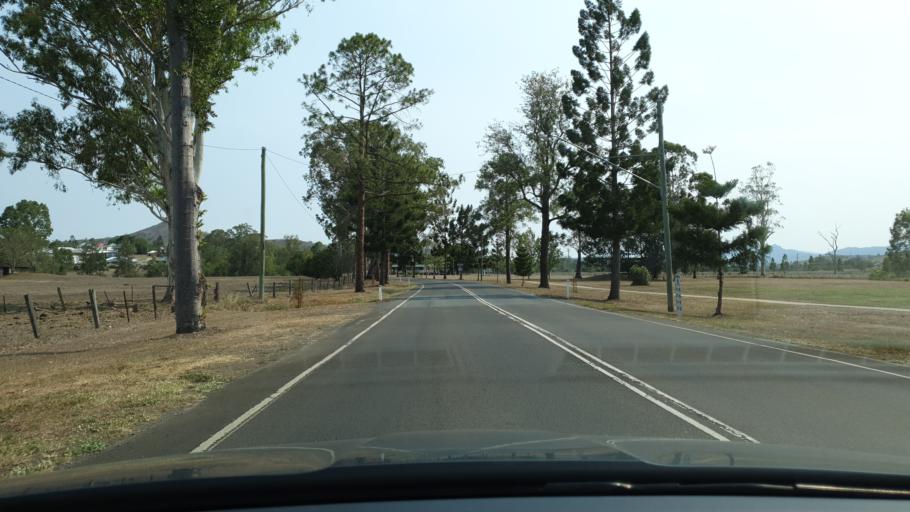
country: AU
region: Queensland
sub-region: Ipswich
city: Deebing Heights
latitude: -28.0016
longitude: 152.6817
